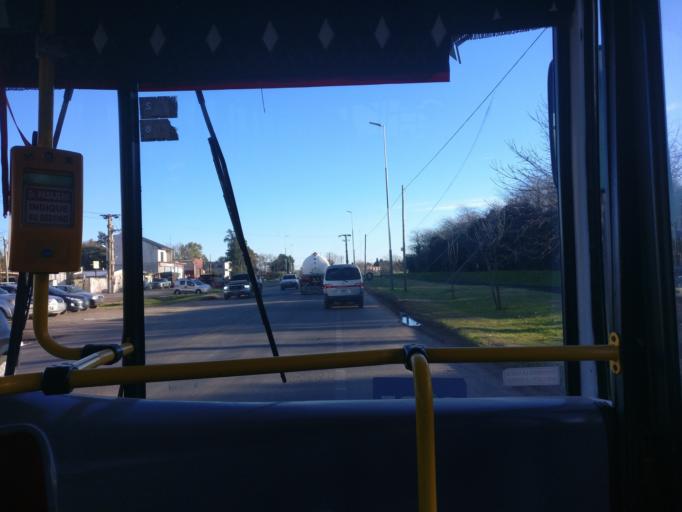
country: AR
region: Buenos Aires
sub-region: Partido de Ezeiza
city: Ezeiza
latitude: -34.9166
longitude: -58.6024
